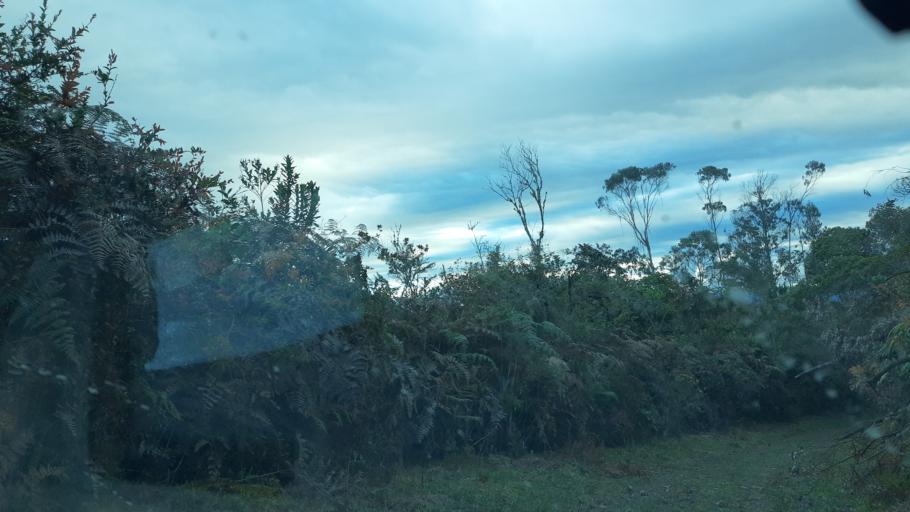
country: CO
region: Boyaca
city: Garagoa
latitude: 5.0829
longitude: -73.3174
